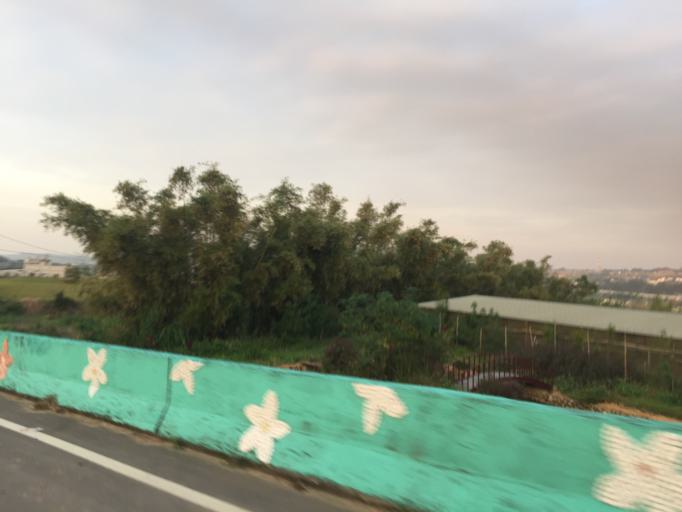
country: TW
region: Taiwan
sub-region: Miaoli
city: Miaoli
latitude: 24.4870
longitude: 120.7758
